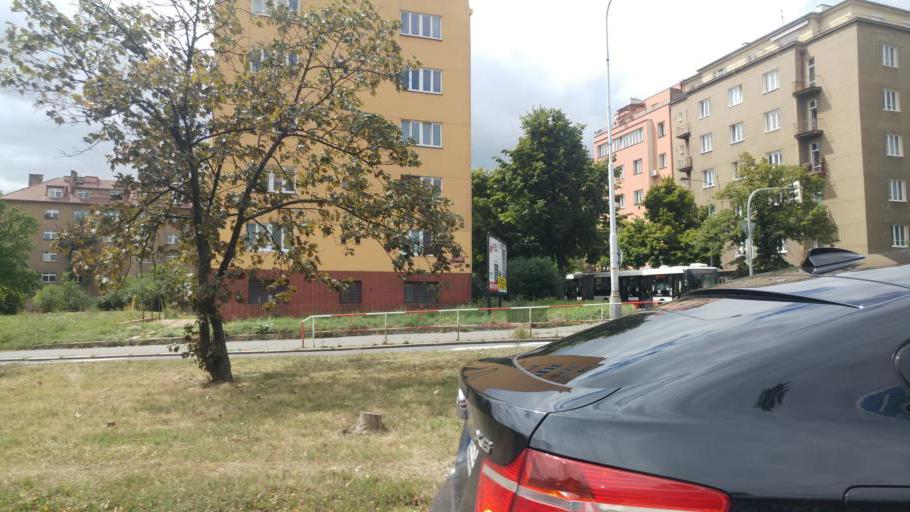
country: CZ
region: Praha
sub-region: Praha 8
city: Karlin
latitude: 50.0718
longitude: 14.4710
